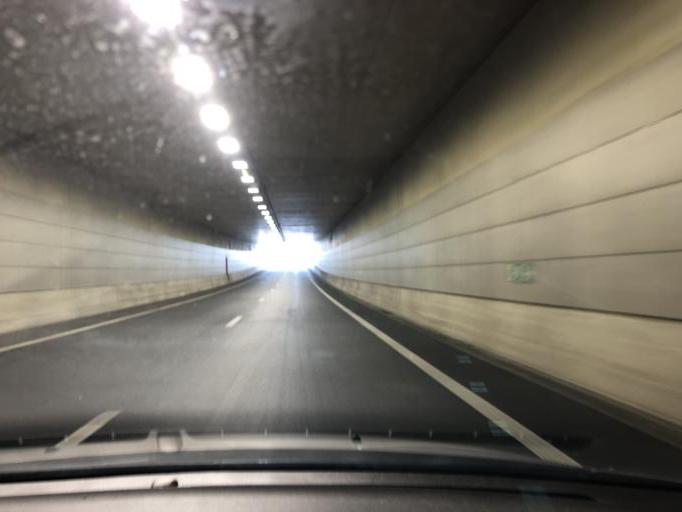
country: NL
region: North Holland
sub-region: Gemeente Medemblik
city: Medemblik
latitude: 52.6915
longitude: 5.1584
